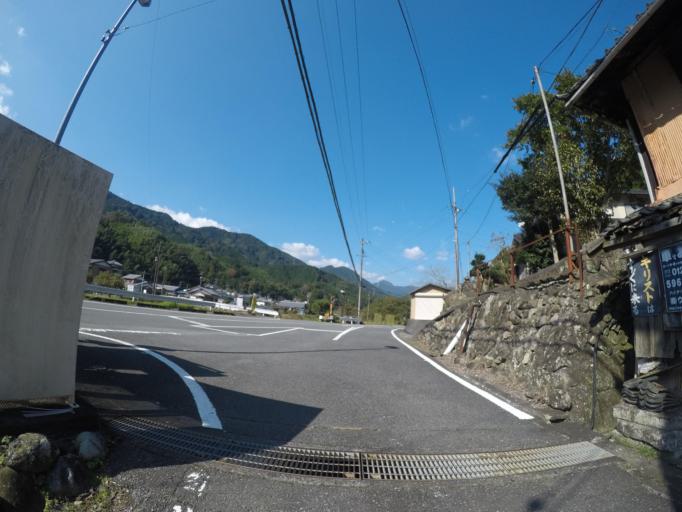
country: JP
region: Shizuoka
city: Fujinomiya
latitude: 35.1181
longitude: 138.4819
